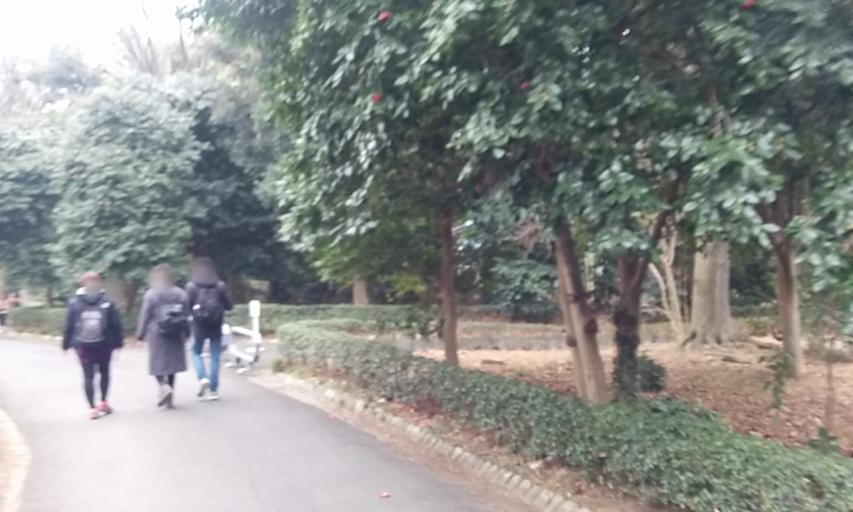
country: JP
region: Tokyo
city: Tokyo
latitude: 35.6847
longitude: 139.7564
